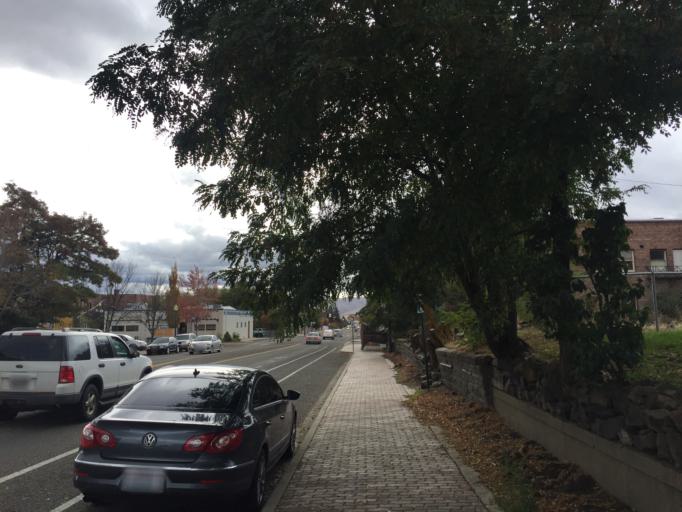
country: US
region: Washington
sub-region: Kittitas County
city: Ellensburg
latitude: 46.9961
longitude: -120.5502
